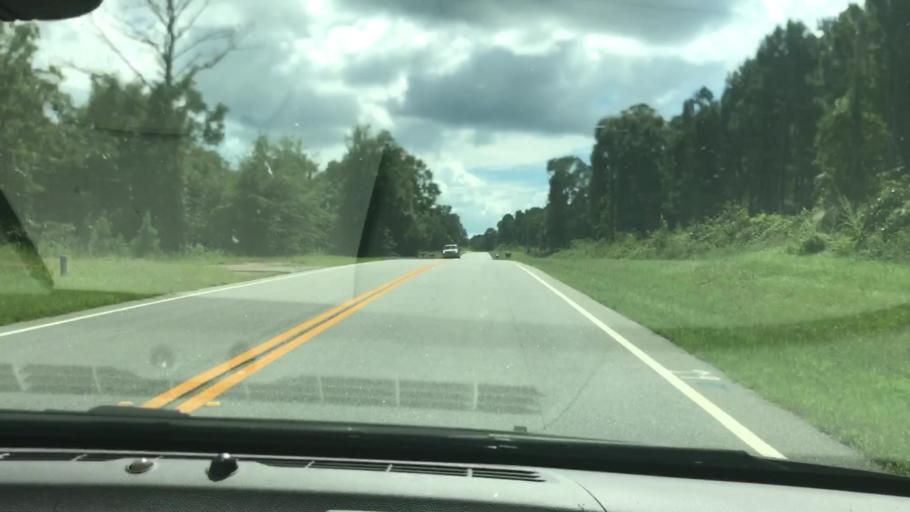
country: US
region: Georgia
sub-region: Quitman County
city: Georgetown
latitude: 31.8247
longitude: -85.0901
